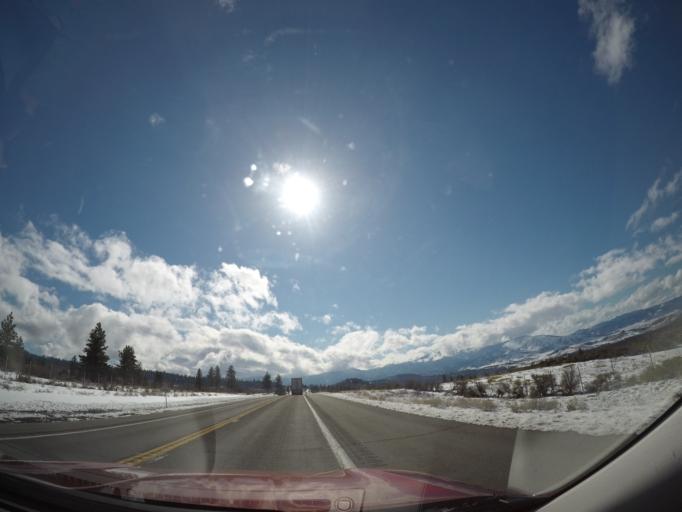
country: US
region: California
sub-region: Siskiyou County
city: Weed
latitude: 41.4930
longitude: -122.3336
